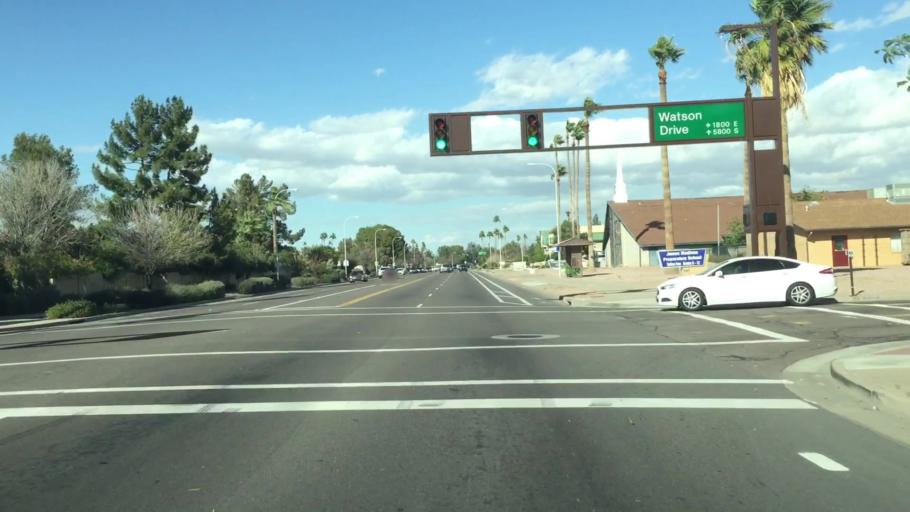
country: US
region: Arizona
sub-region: Maricopa County
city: Tempe
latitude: 33.3693
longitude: -111.9112
